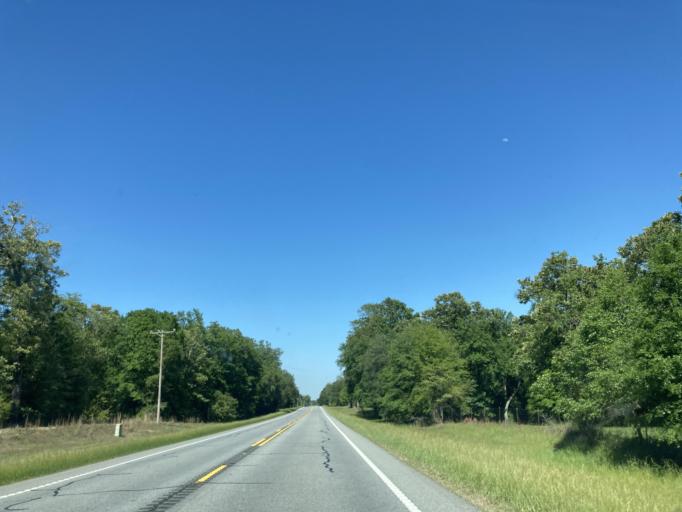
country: US
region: Georgia
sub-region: Baker County
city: Newton
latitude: 31.2810
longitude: -84.3724
